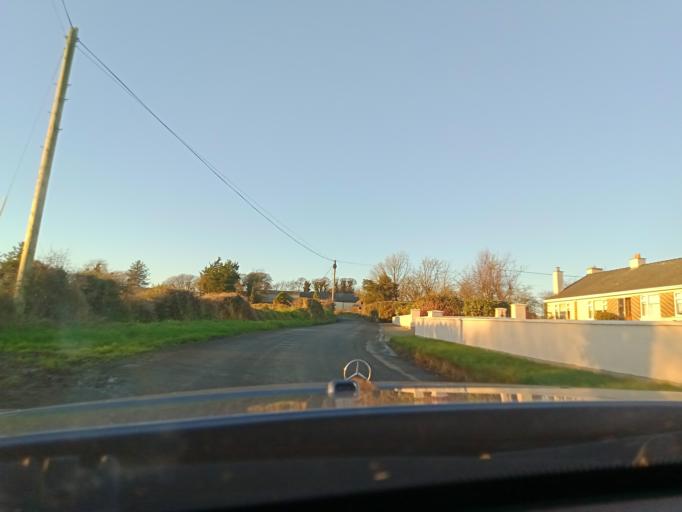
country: IE
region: Munster
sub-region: Waterford
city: Waterford
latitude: 52.3722
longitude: -7.1283
